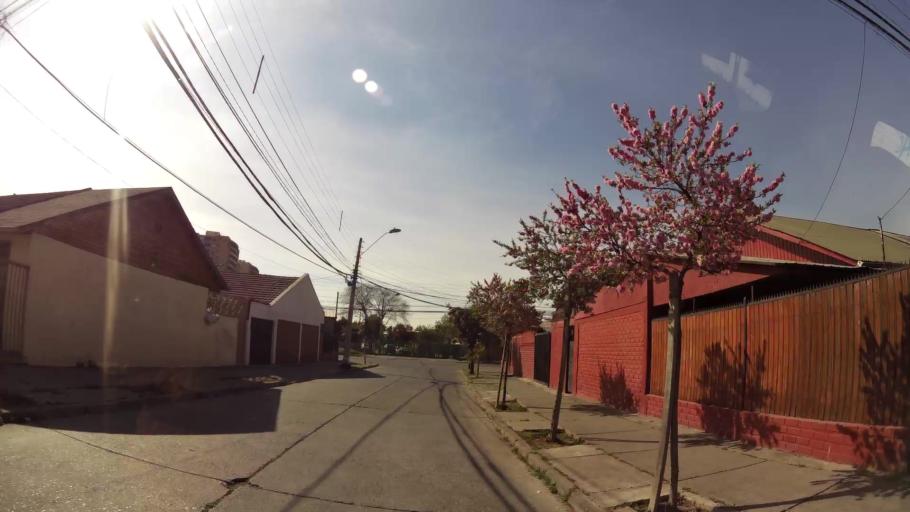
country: CL
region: Santiago Metropolitan
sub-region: Provincia de Santiago
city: La Pintana
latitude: -33.5288
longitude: -70.5930
